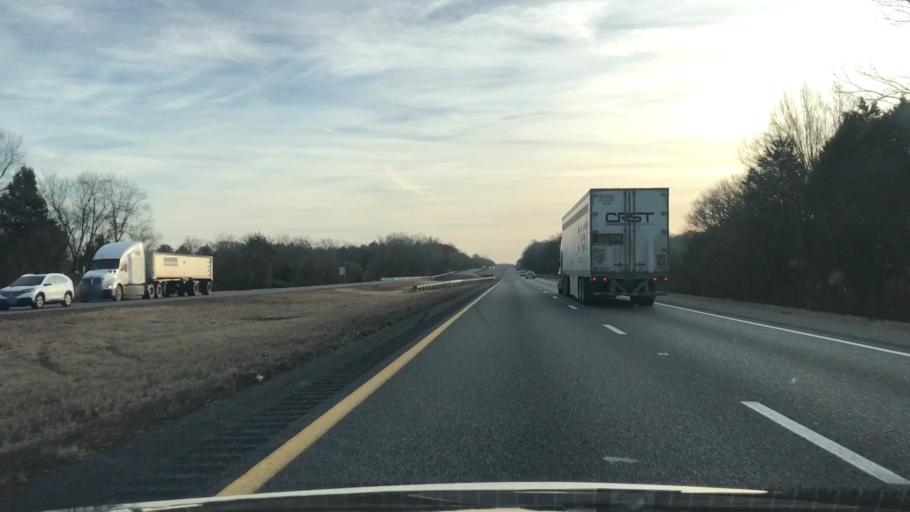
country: US
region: Tennessee
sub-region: Wilson County
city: Lebanon
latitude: 36.1933
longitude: -86.2401
